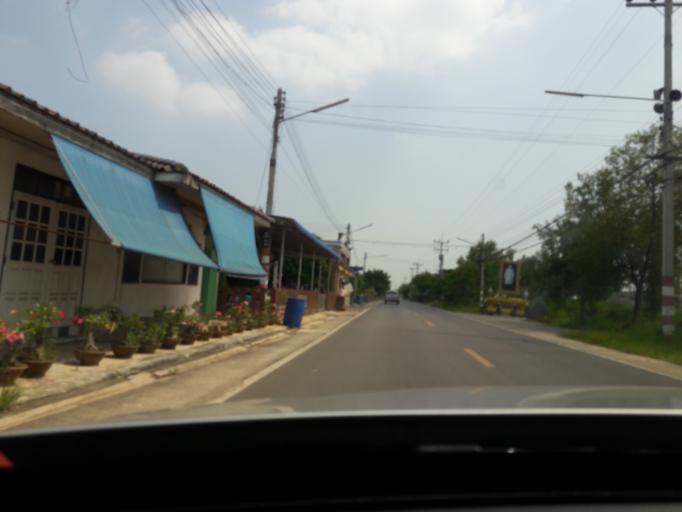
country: TH
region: Samut Songkhram
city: Amphawa
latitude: 13.3503
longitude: 99.9373
